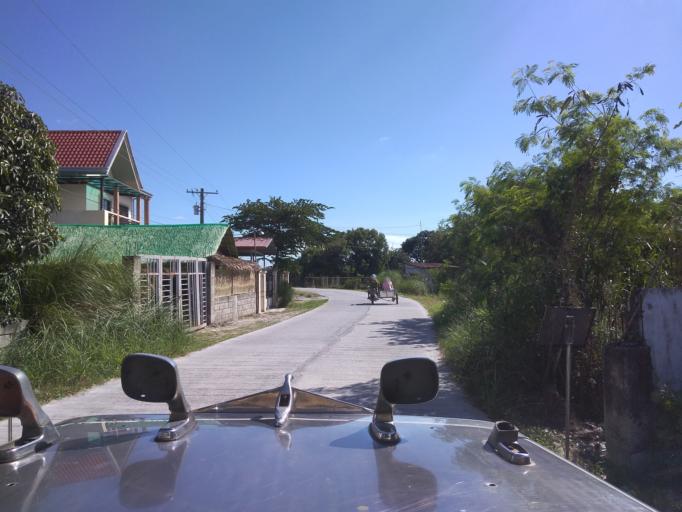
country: PH
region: Central Luzon
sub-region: Province of Pampanga
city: Bacolor
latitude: 15.0252
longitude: 120.6368
